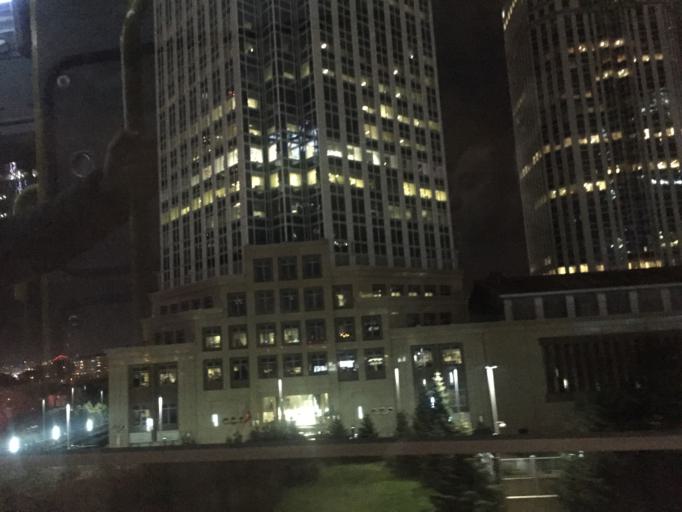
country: TR
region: Istanbul
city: Sisli
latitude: 41.0824
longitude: 29.0107
